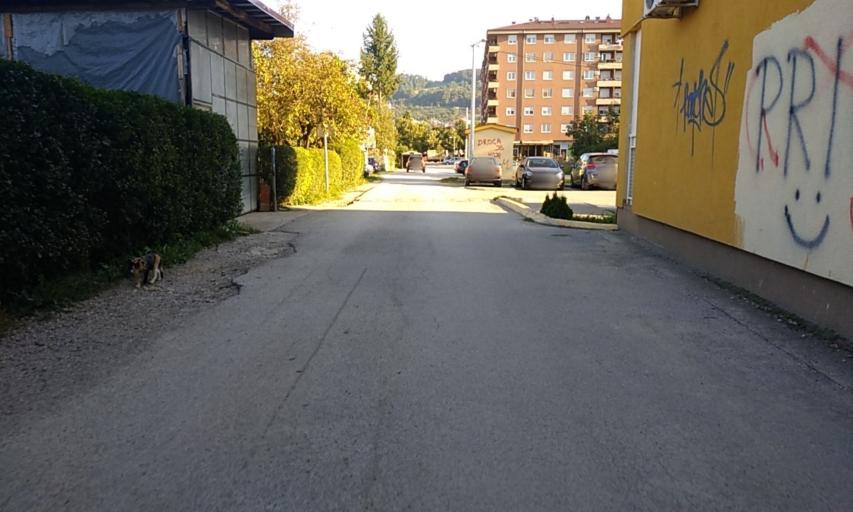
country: BA
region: Republika Srpska
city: Starcevica
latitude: 44.7650
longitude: 17.2039
